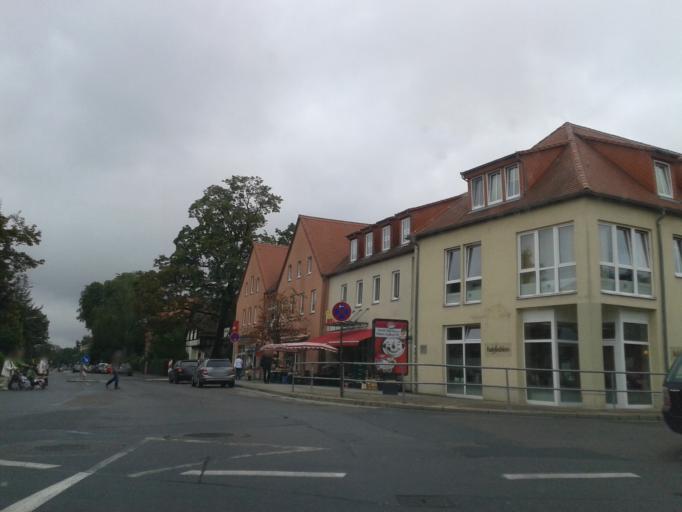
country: DE
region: Saxony
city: Dresden
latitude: 51.0157
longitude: 13.7642
